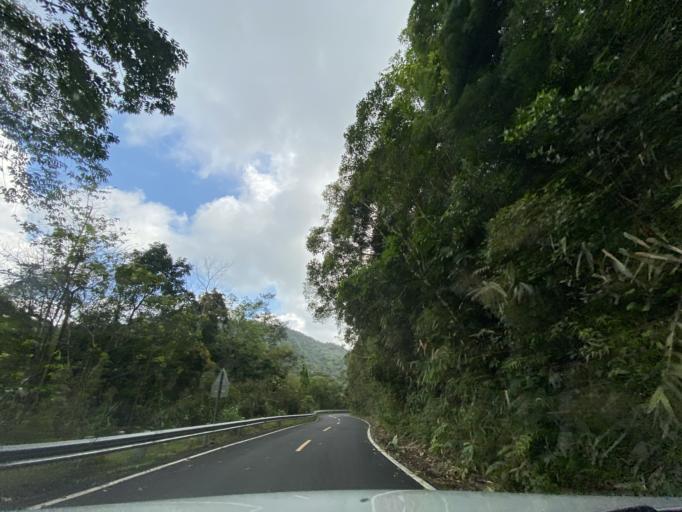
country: CN
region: Hainan
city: Diaoluoshan
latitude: 18.7043
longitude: 109.8821
